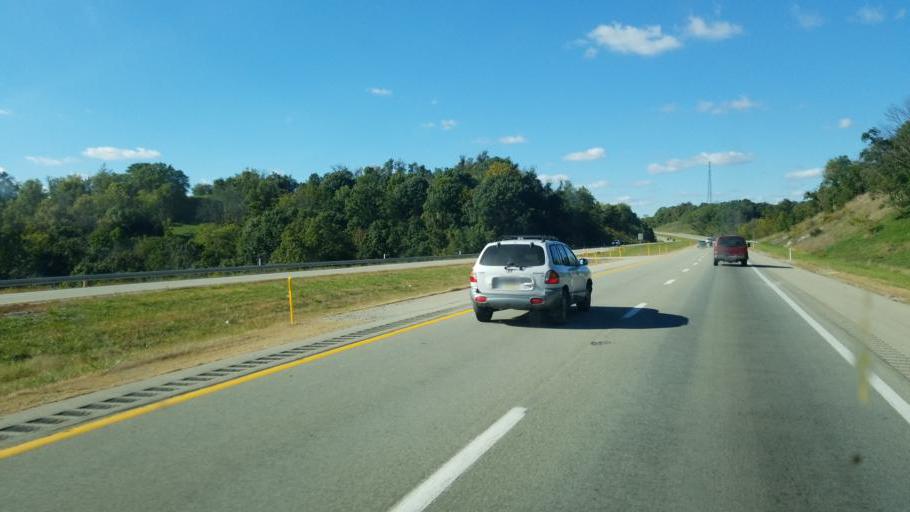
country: US
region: Pennsylvania
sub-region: Greene County
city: Morrisville
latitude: 39.8445
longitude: -80.1145
